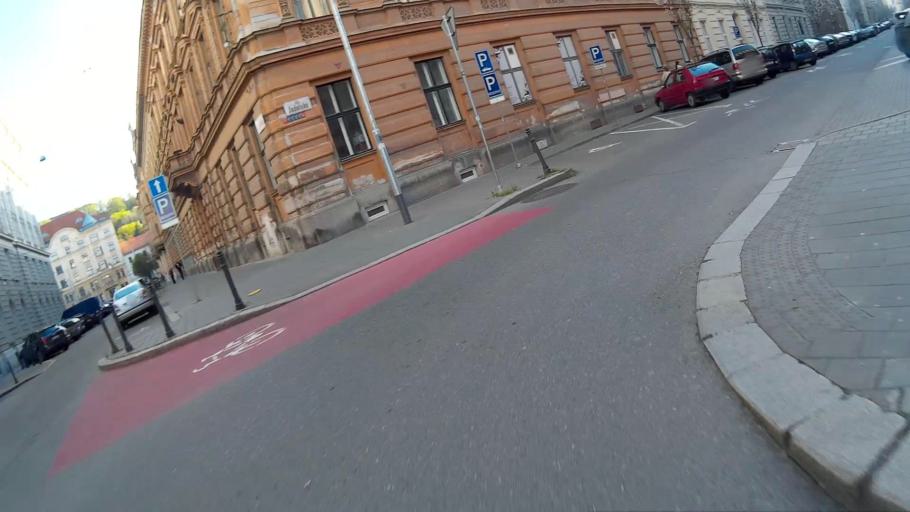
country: CZ
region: South Moravian
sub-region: Mesto Brno
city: Brno
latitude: 49.1978
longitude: 16.6021
